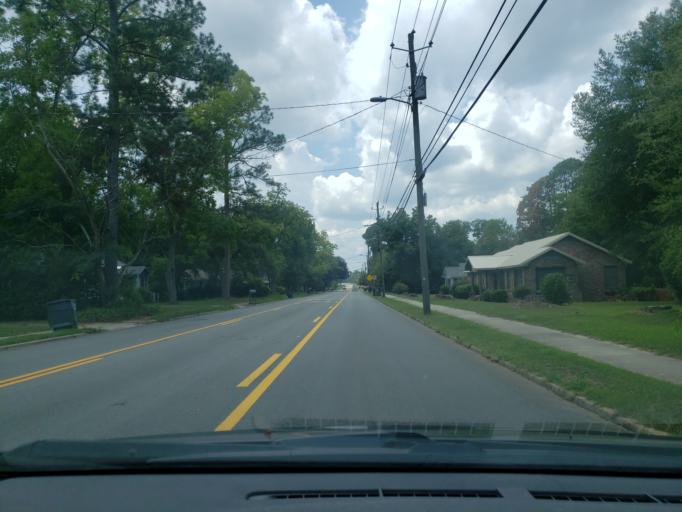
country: US
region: Georgia
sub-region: Bleckley County
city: Cochran
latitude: 32.3807
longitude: -83.3616
